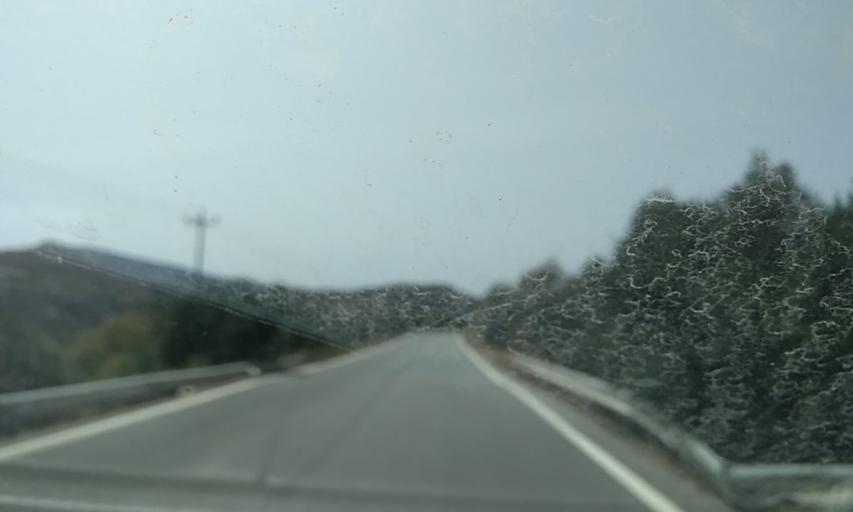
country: GR
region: Crete
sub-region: Nomos Lasithiou
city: Siteia
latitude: 35.1166
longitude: 26.0619
